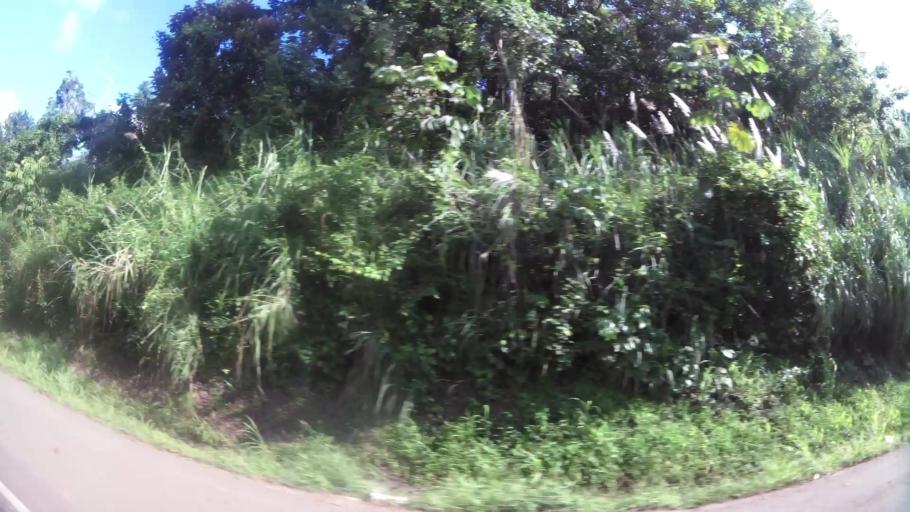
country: PA
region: Panama
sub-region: Distrito Arraijan
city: Arraijan
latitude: 8.9565
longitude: -79.6569
